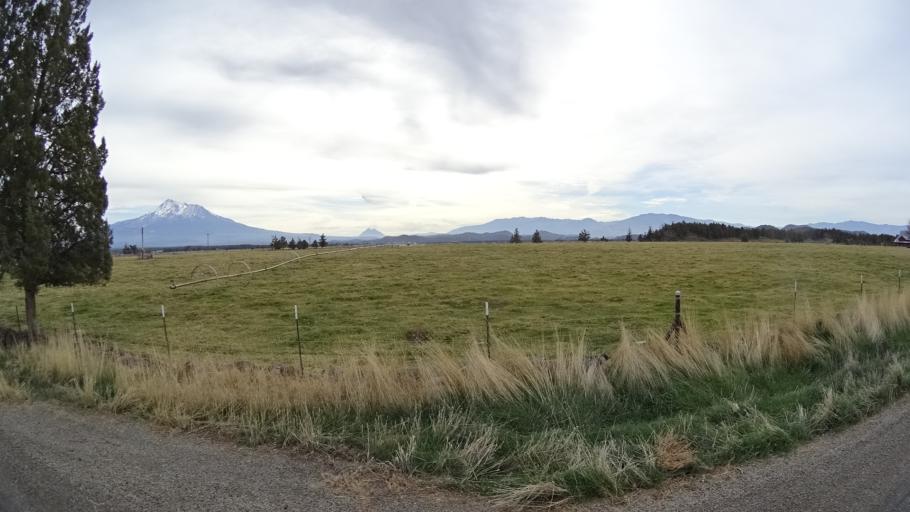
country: US
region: California
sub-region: Siskiyou County
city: Montague
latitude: 41.6241
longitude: -122.4107
